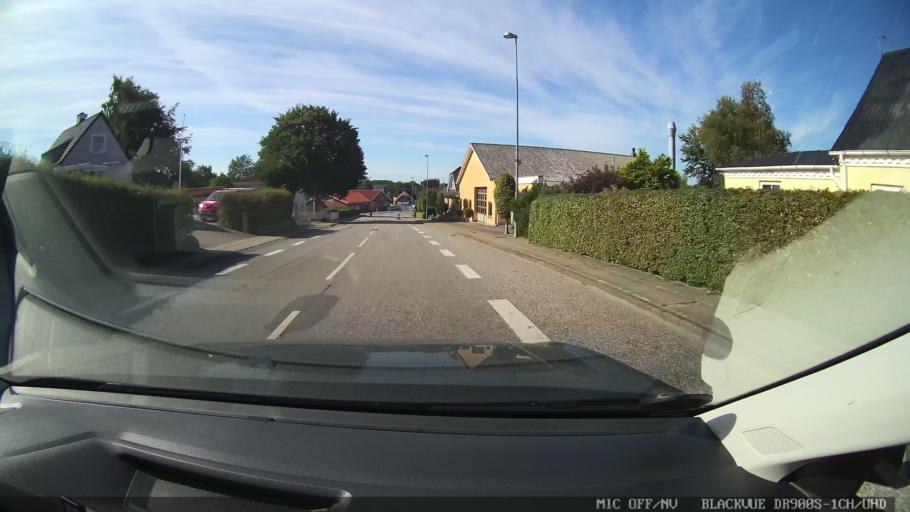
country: DK
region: North Denmark
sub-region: Mariagerfjord Kommune
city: Hobro
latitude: 56.6745
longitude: 9.8562
